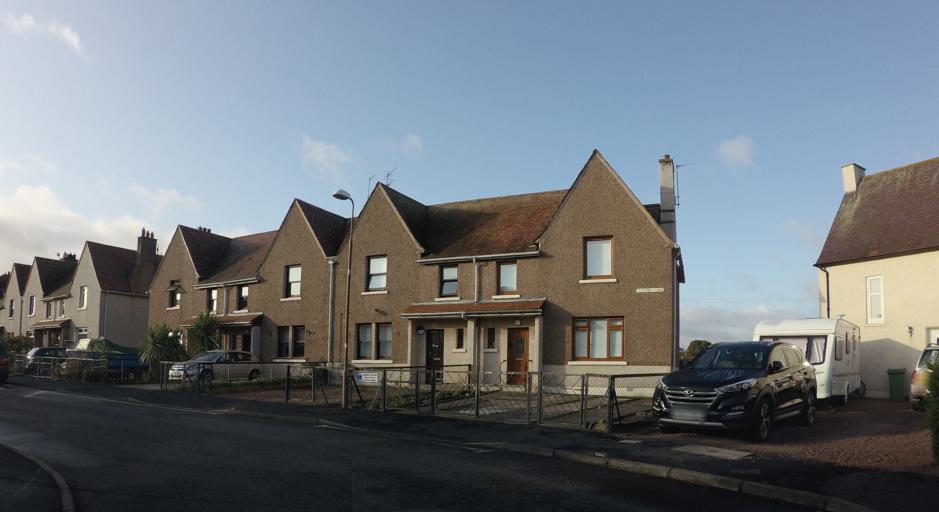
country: GB
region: Scotland
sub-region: East Lothian
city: Musselburgh
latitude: 55.9191
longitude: -3.0370
